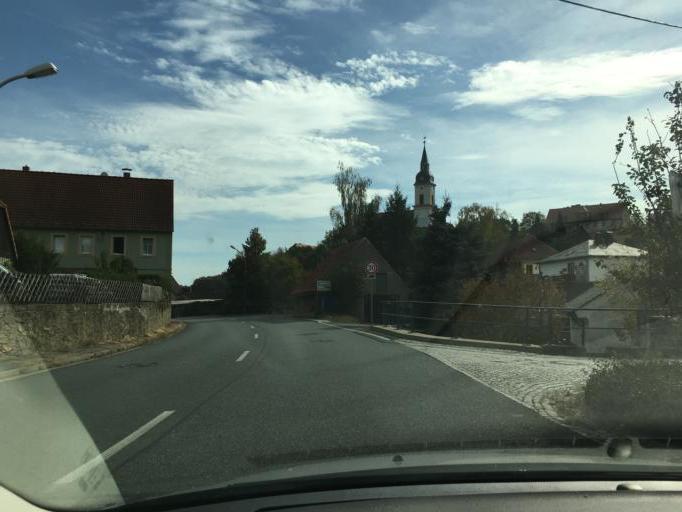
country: DE
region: Saxony
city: Meissen
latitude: 51.2015
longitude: 13.4027
